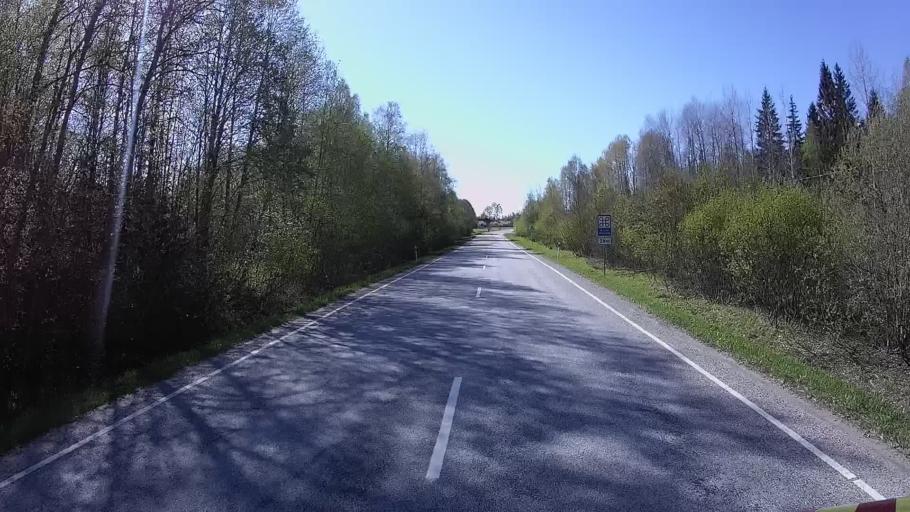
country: EE
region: Raplamaa
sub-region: Jaervakandi vald
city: Jarvakandi
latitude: 58.7949
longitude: 24.8175
